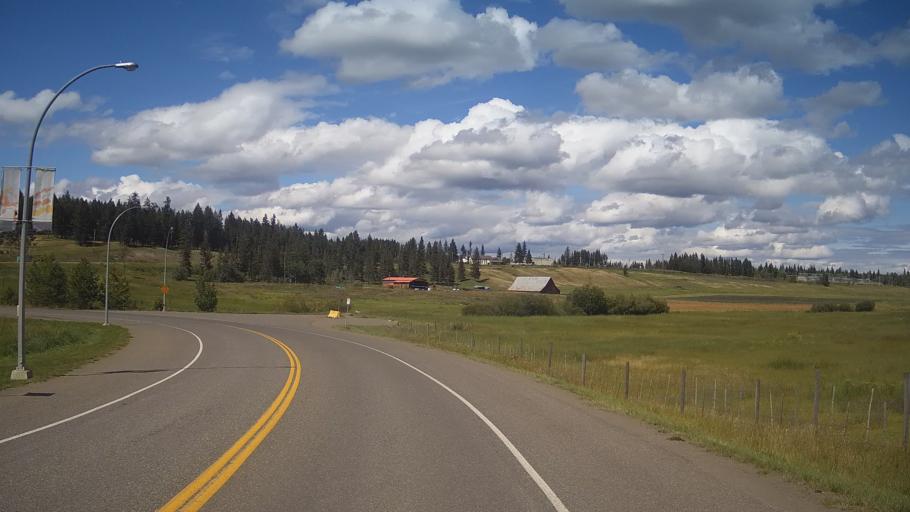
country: CA
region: British Columbia
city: Cache Creek
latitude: 51.6493
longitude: -121.2937
